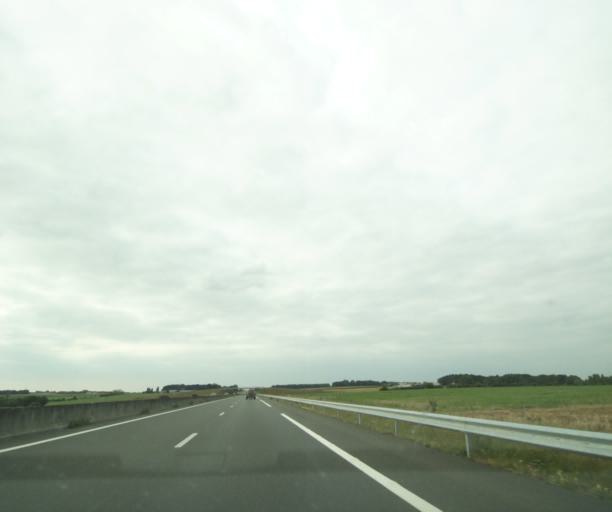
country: FR
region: Centre
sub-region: Departement d'Indre-et-Loire
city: Saint-Paterne-Racan
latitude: 47.6078
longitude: 0.5302
